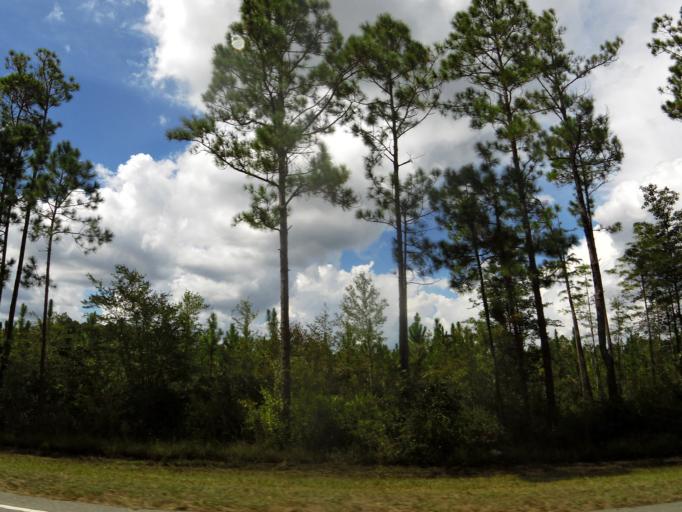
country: US
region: Georgia
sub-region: Brantley County
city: Nahunta
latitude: 31.1259
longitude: -82.0000
